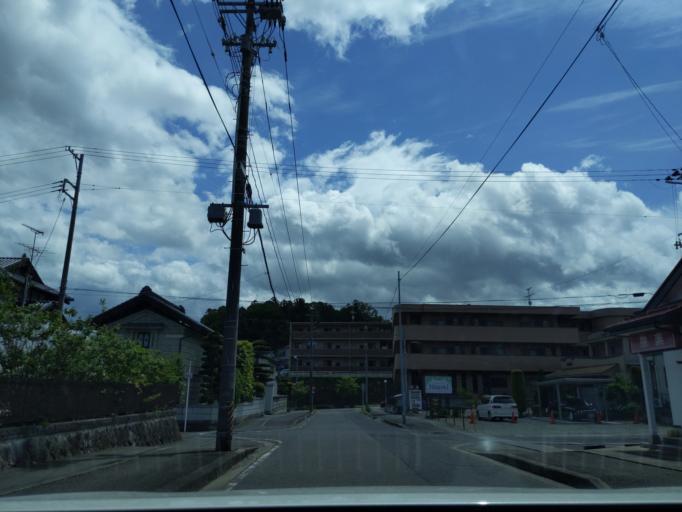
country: JP
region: Fukushima
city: Sukagawa
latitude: 37.3022
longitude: 140.3636
